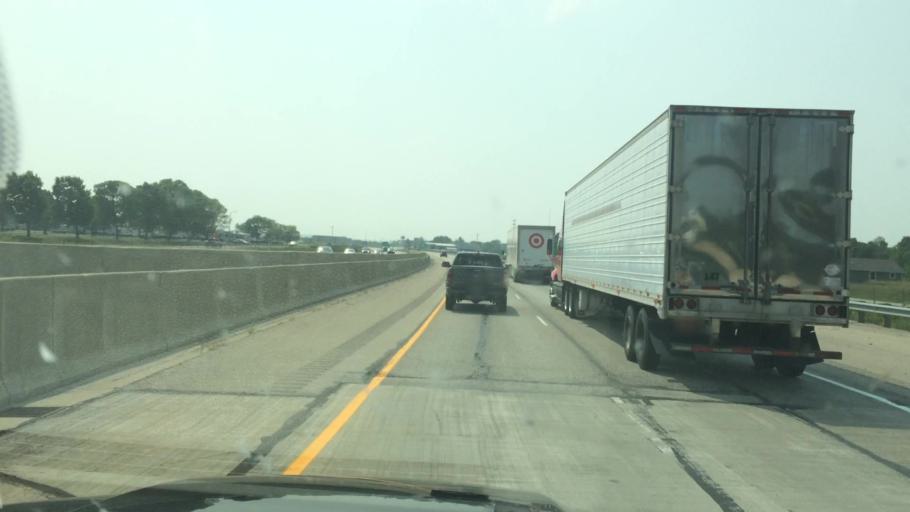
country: US
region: Wisconsin
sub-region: Fond du Lac County
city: Fond du Lac
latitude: 43.7670
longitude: -88.4810
